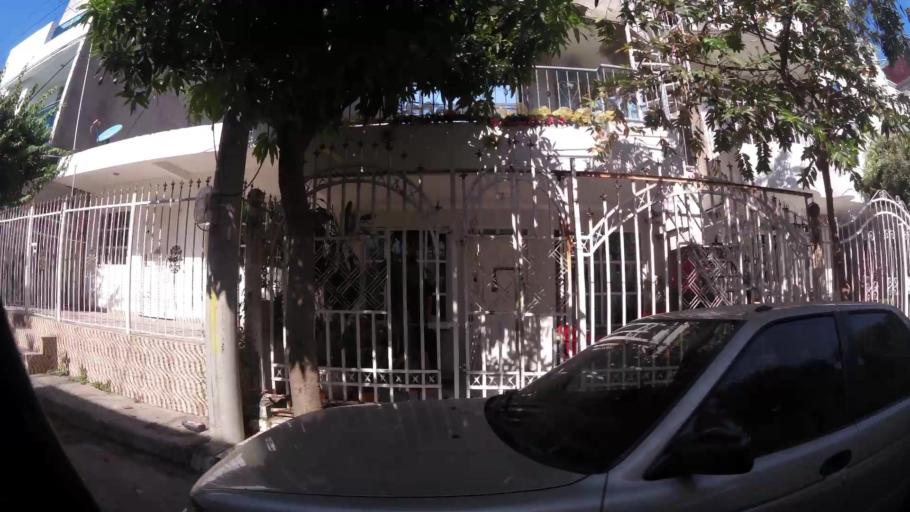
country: CO
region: Bolivar
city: Cartagena
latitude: 10.3860
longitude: -75.4683
